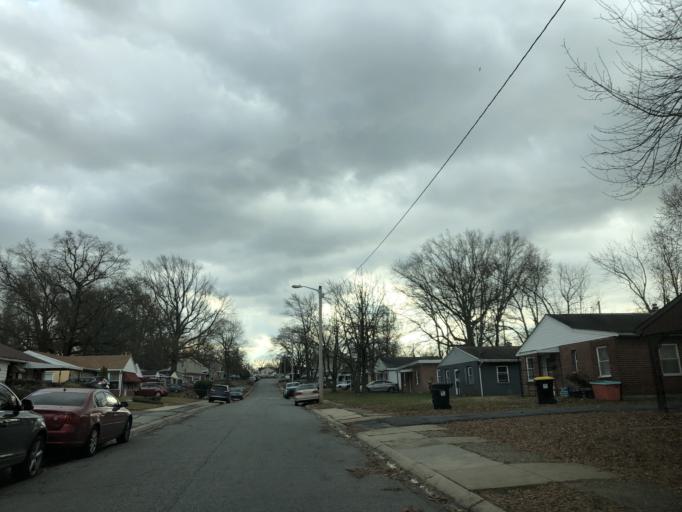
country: US
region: Delaware
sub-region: New Castle County
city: Wilmington
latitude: 39.7112
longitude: -75.5553
